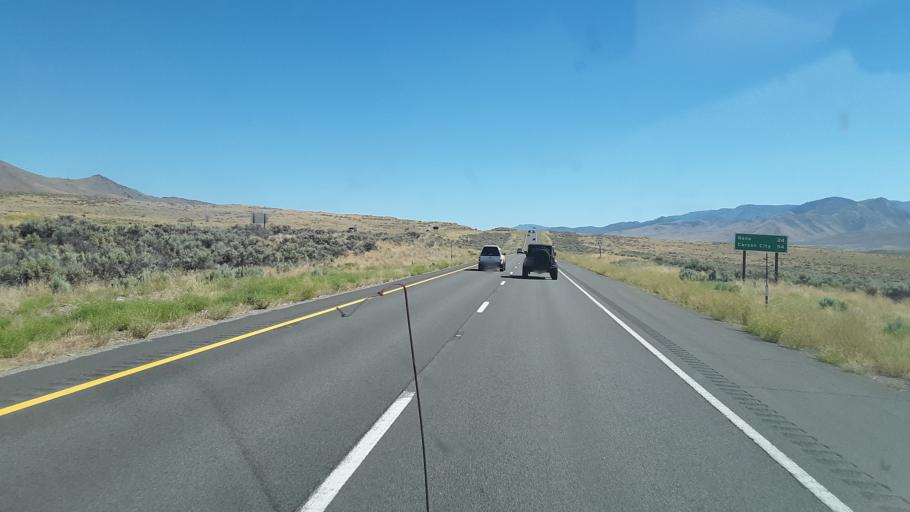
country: US
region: Nevada
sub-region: Washoe County
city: Cold Springs
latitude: 39.7678
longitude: -120.0392
